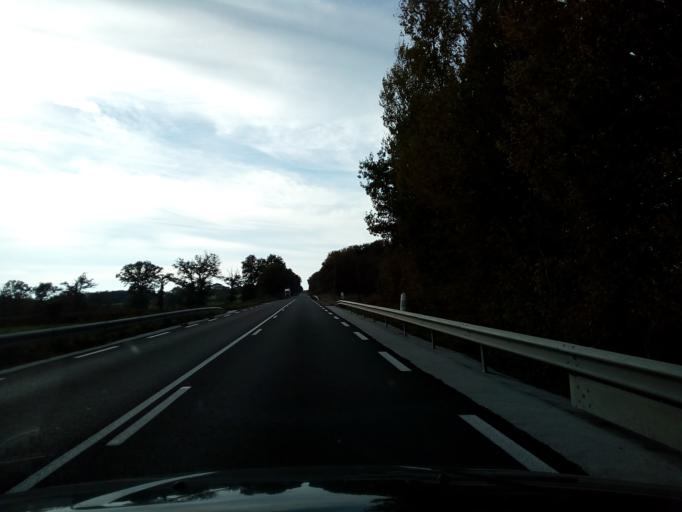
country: FR
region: Limousin
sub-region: Departement de la Haute-Vienne
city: Magnac-Laval
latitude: 46.1838
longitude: 1.1809
